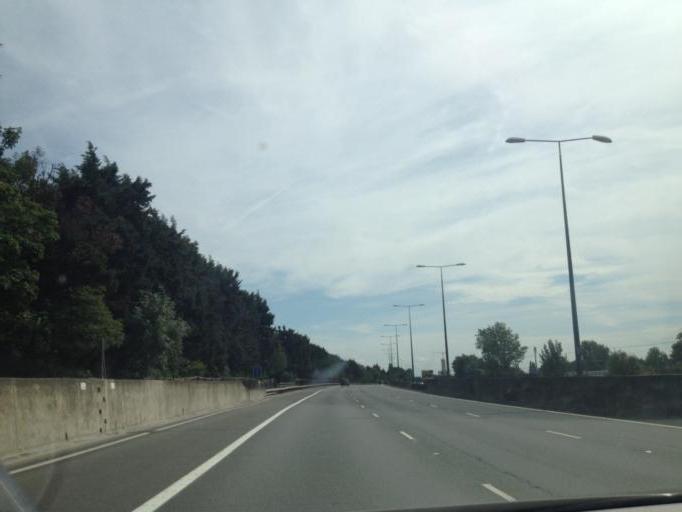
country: GB
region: England
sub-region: Greater London
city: Hendon
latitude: 51.5940
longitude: -0.2354
